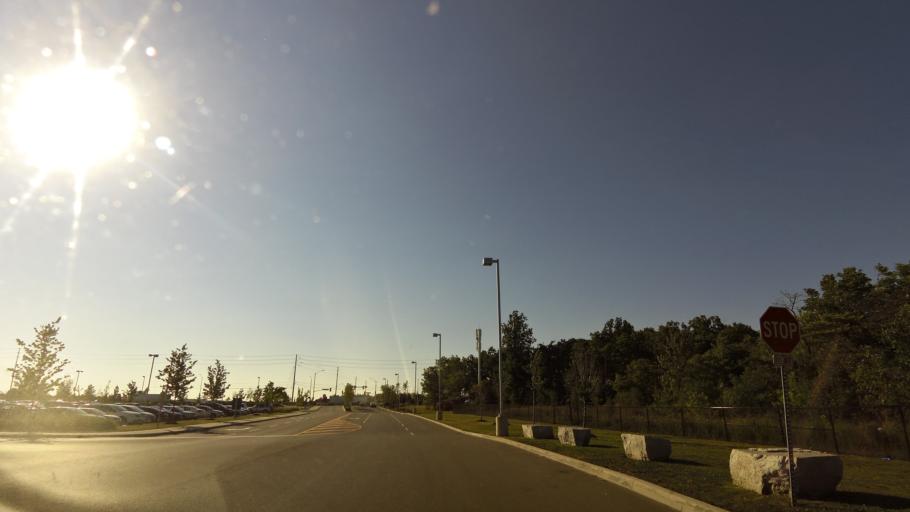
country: CA
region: Ontario
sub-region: Halton
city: Milton
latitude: 43.5771
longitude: -79.8284
